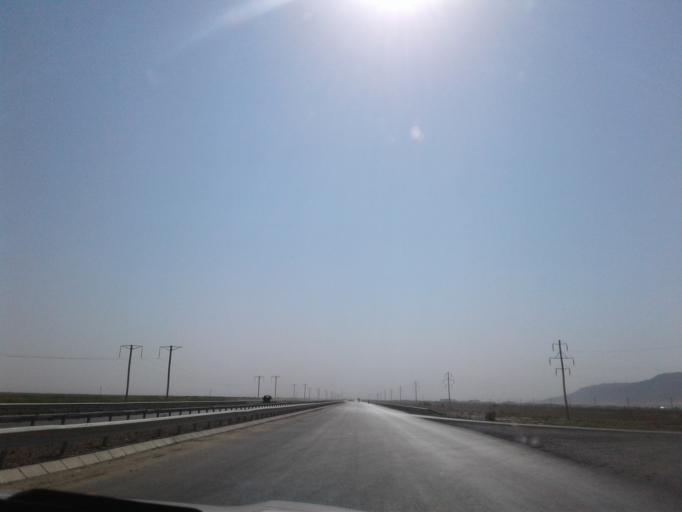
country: TM
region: Balkan
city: Gazanjyk
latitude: 39.2742
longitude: 55.5051
